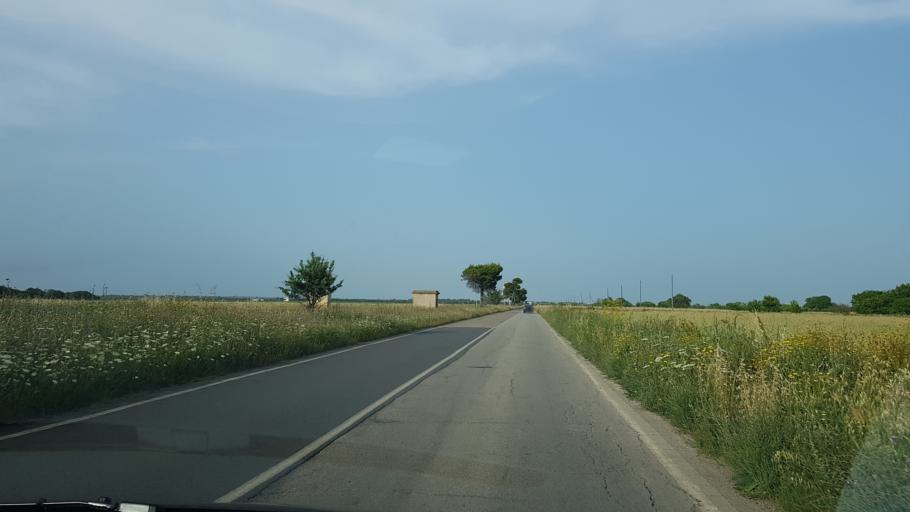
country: IT
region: Apulia
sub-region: Provincia di Brindisi
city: San Pancrazio Salentino
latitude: 40.4273
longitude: 17.8658
